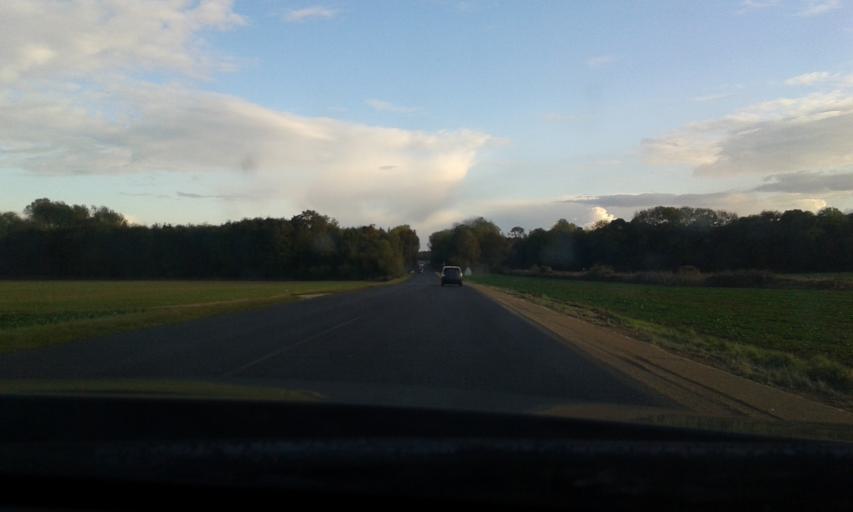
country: FR
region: Centre
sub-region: Departement d'Eure-et-Loir
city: Le Coudray
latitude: 48.4075
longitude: 1.5448
